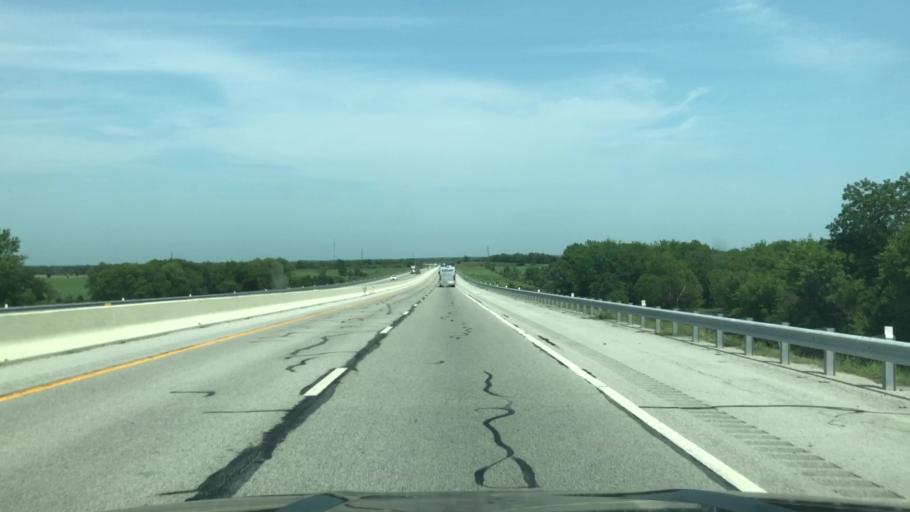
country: US
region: Oklahoma
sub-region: Rogers County
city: Chelsea
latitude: 36.4898
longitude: -95.3006
